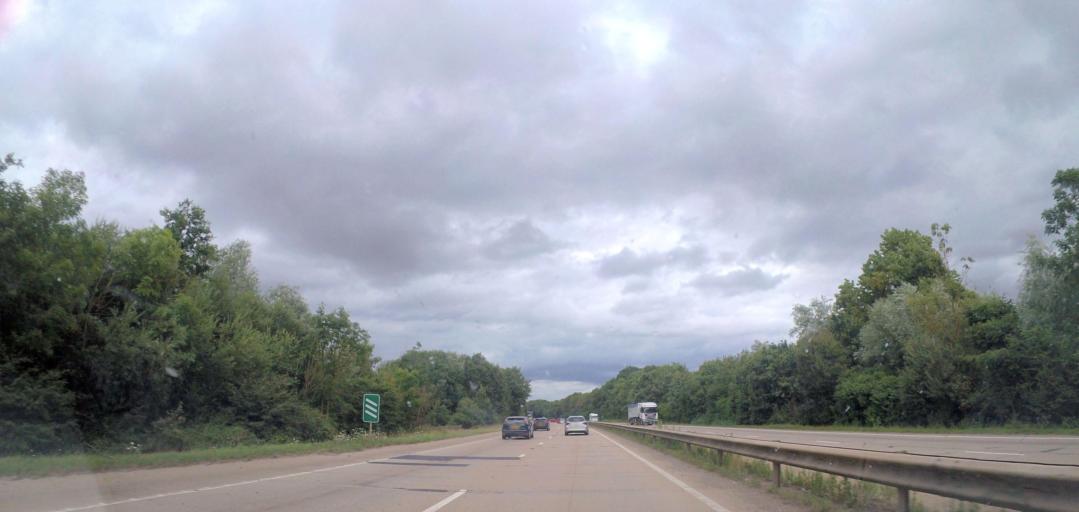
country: GB
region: England
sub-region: Norfolk
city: Hethersett
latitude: 52.5614
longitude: 1.1322
